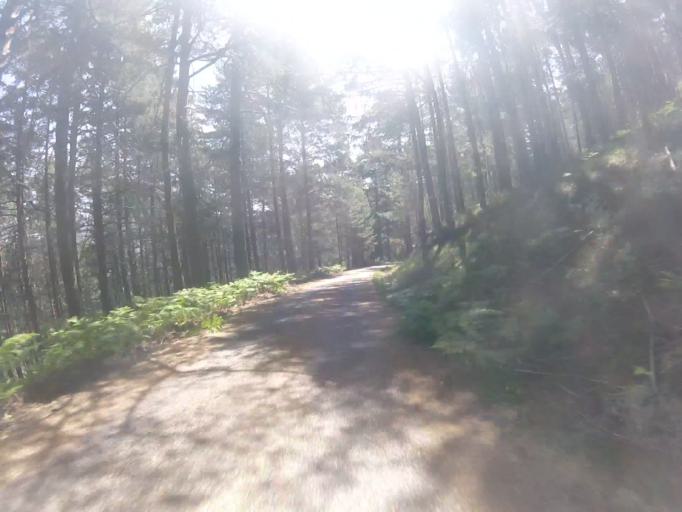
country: ES
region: Madrid
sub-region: Provincia de Madrid
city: Cercedilla
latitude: 40.8090
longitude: -4.0458
